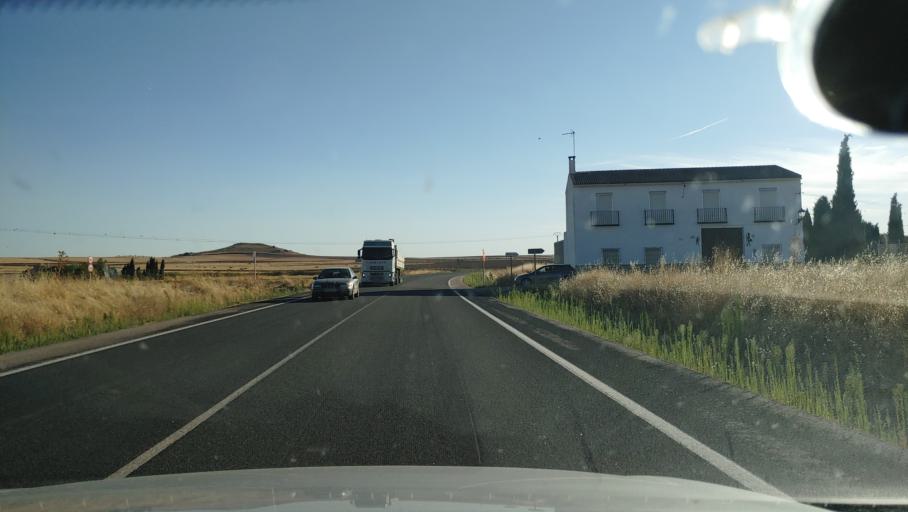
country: ES
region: Castille-La Mancha
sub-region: Provincia de Ciudad Real
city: Fuenllana
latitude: 38.7543
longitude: -2.9544
